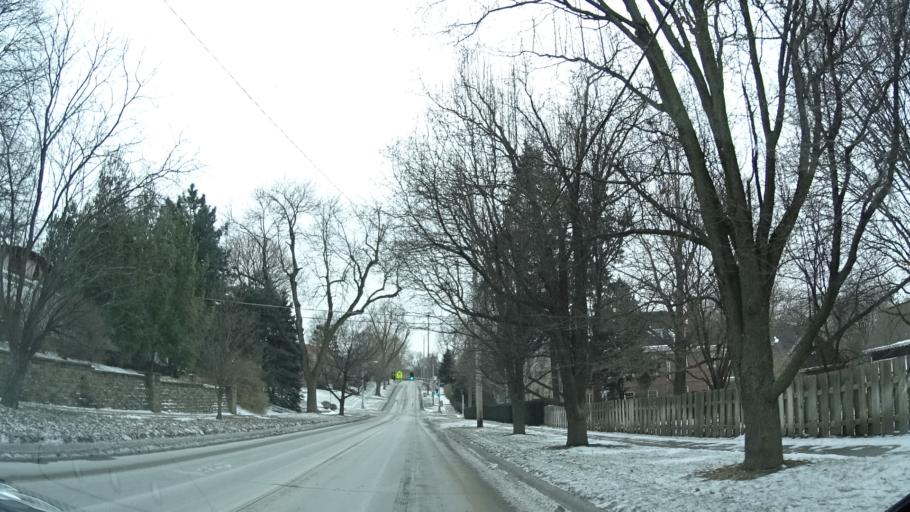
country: US
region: Nebraska
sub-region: Douglas County
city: Omaha
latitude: 41.2632
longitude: -95.9951
